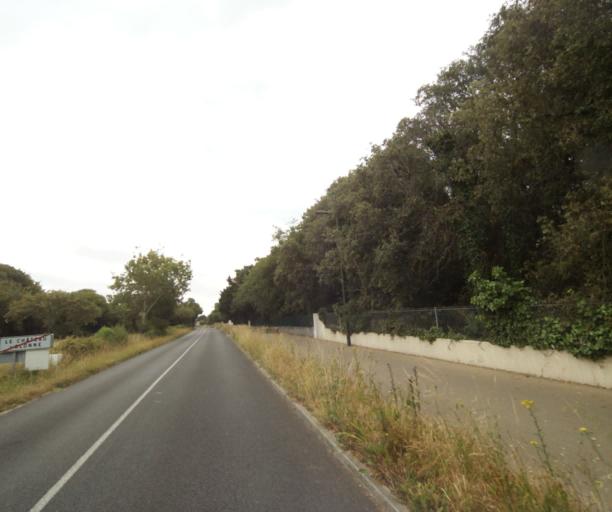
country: FR
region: Pays de la Loire
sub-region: Departement de la Vendee
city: Chateau-d'Olonne
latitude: 46.4638
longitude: -1.7263
